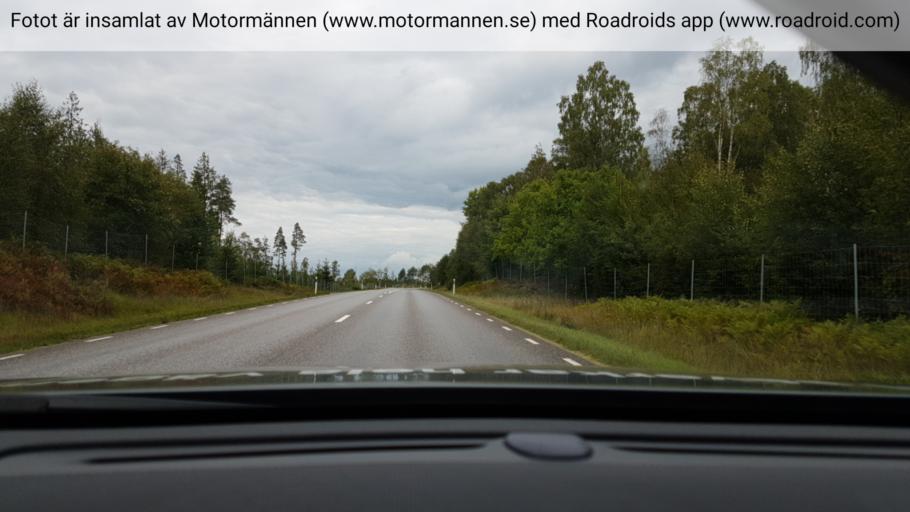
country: SE
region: Halland
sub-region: Hylte Kommun
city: Hyltebruk
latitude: 57.0068
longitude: 13.2313
